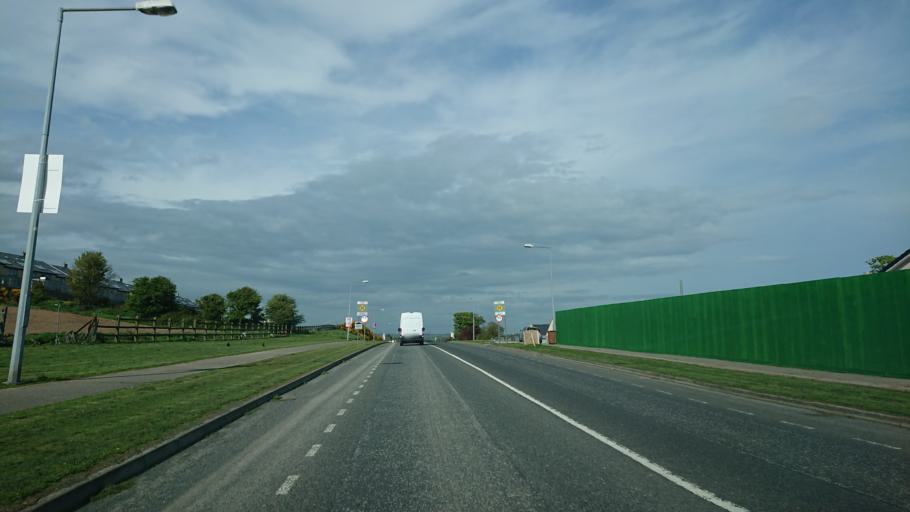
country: IE
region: Munster
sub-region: Waterford
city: Waterford
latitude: 52.2589
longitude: -7.1531
